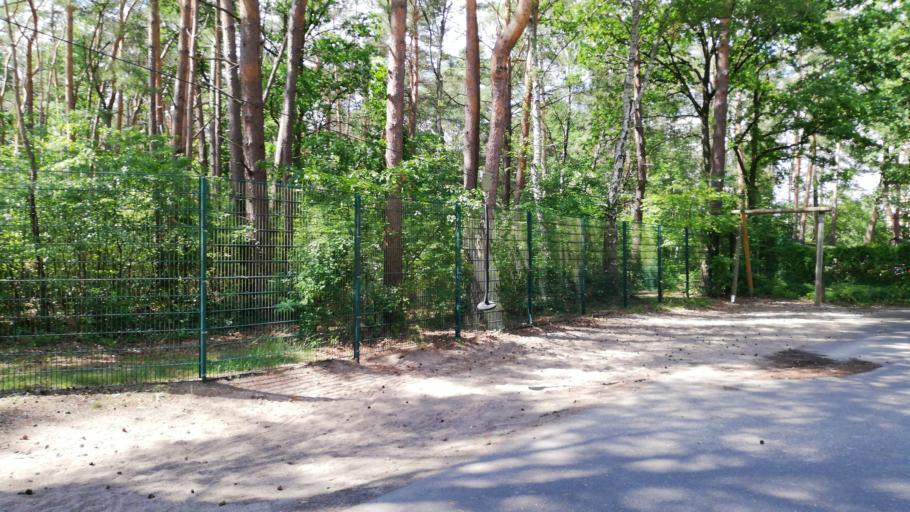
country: DE
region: Lower Saxony
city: Neu Wulmstorf
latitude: 53.4668
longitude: 9.8591
